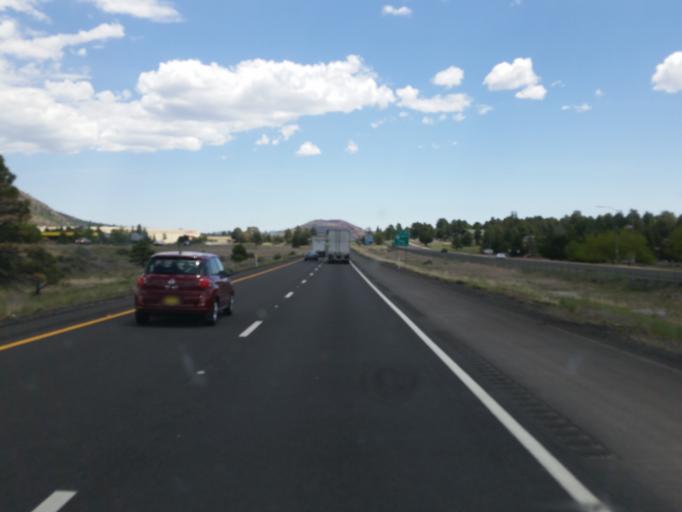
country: US
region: Arizona
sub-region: Coconino County
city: Flagstaff
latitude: 35.2039
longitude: -111.6051
